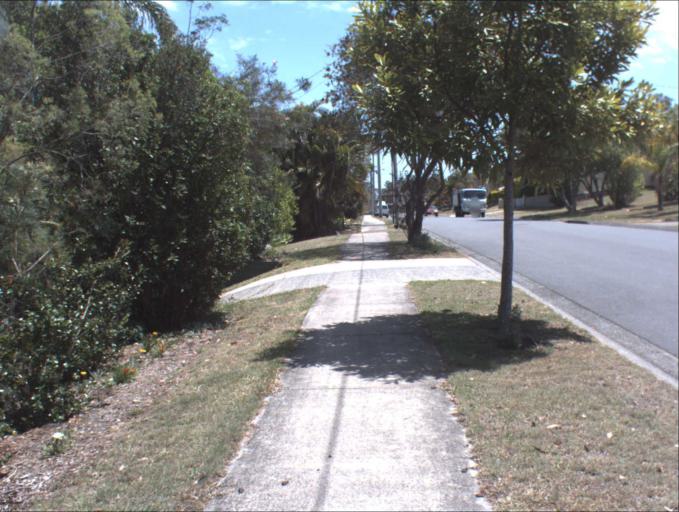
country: AU
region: Queensland
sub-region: Logan
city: Rochedale South
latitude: -27.5967
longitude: 153.1436
